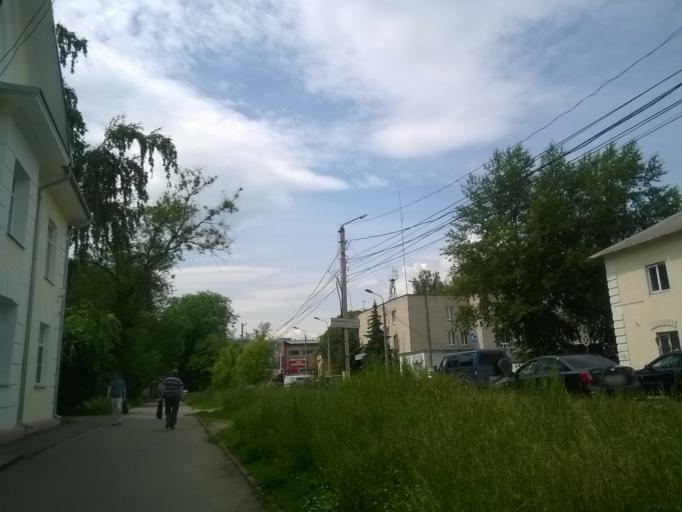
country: RU
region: Kursk
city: Kursk
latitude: 51.6748
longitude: 36.1492
